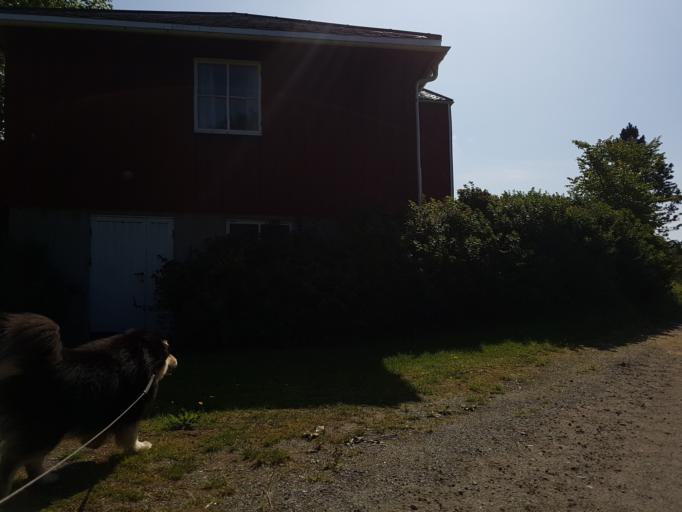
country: NO
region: Sor-Trondelag
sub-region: Agdenes
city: Lensvik
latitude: 63.6318
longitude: 9.8400
